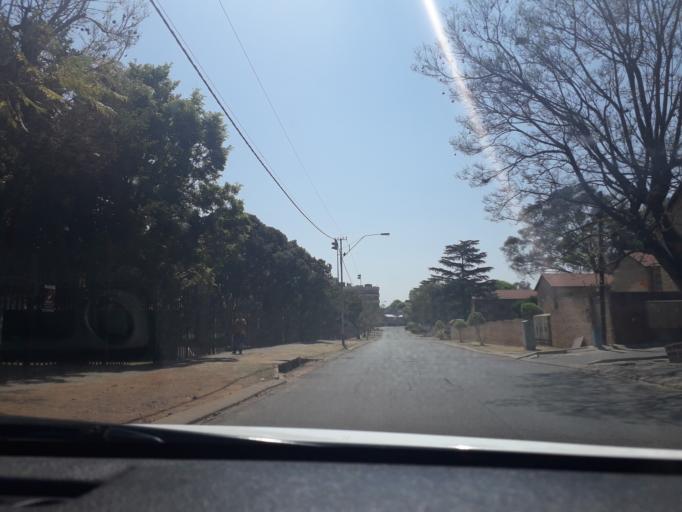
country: ZA
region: Gauteng
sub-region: City of Johannesburg Metropolitan Municipality
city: Roodepoort
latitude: -26.1303
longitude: 27.9663
